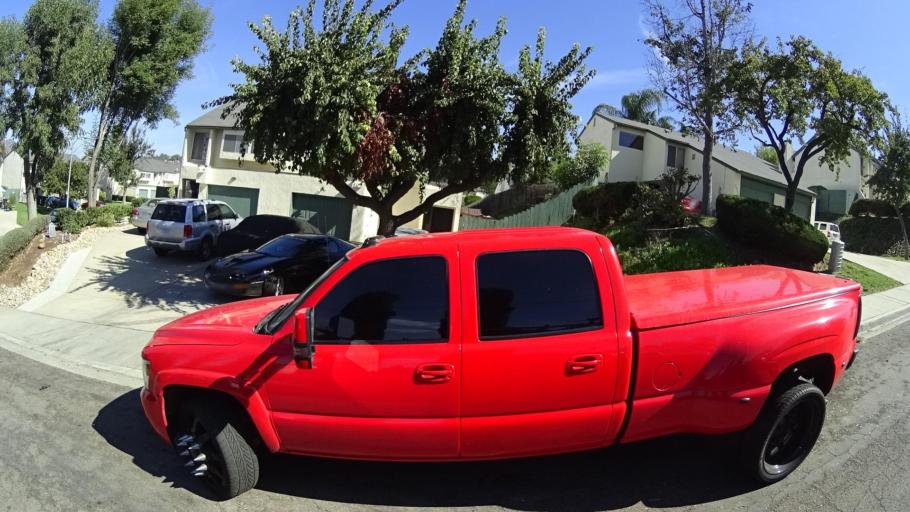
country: US
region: California
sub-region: San Diego County
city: Spring Valley
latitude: 32.7265
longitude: -117.0114
